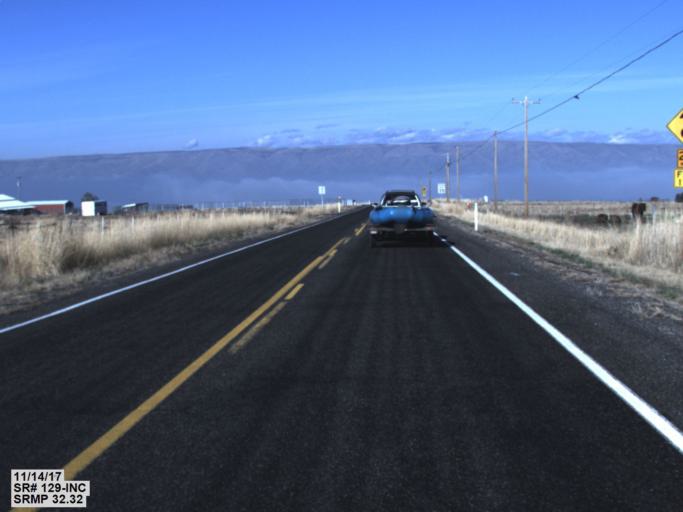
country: US
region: Washington
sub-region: Asotin County
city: Asotin
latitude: 46.3237
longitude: -117.0412
